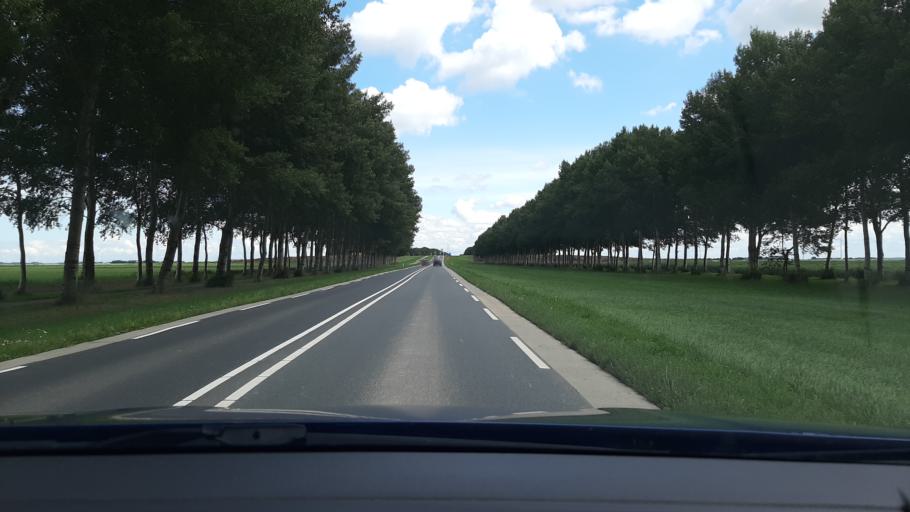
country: NL
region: North Holland
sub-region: Gemeente Huizen
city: Huizen
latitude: 52.3463
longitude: 5.3287
